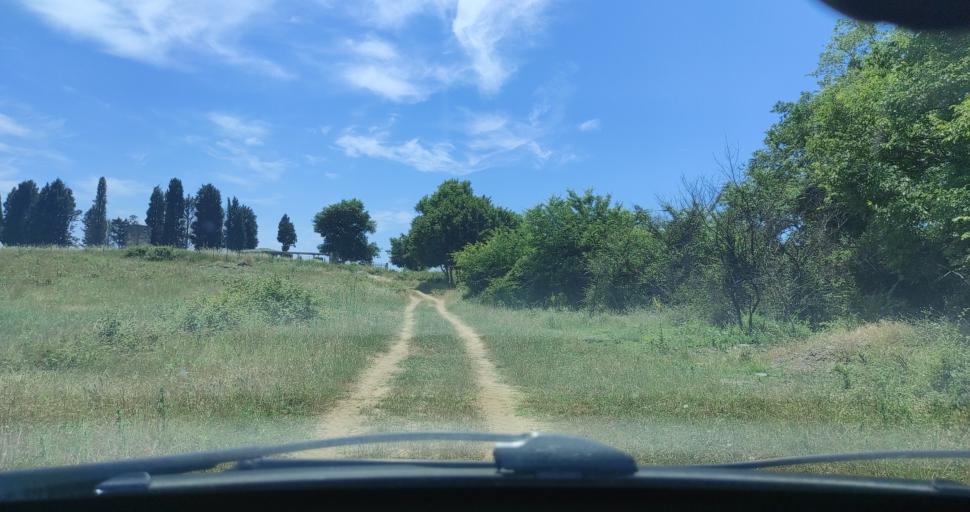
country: AL
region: Shkoder
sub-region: Rrethi i Shkodres
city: Velipoje
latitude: 41.8841
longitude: 19.3846
